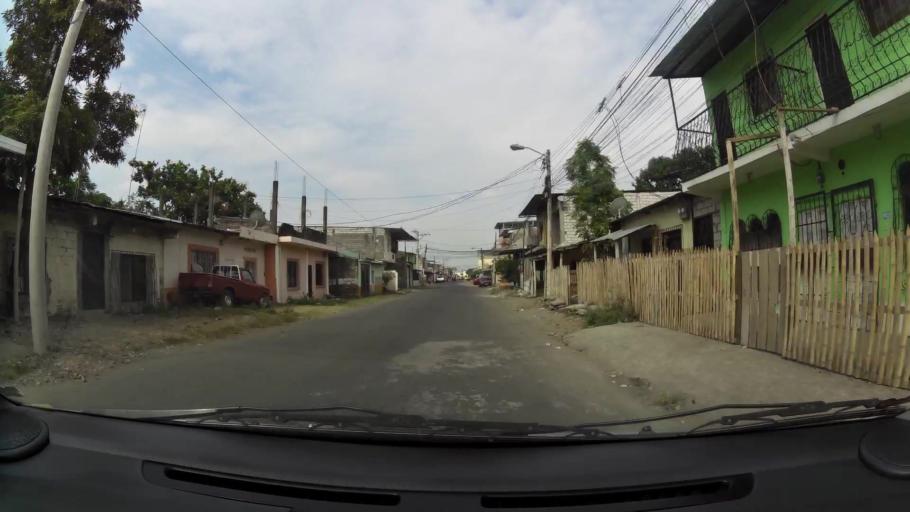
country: EC
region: Guayas
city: Guayaquil
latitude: -2.2573
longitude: -79.9058
